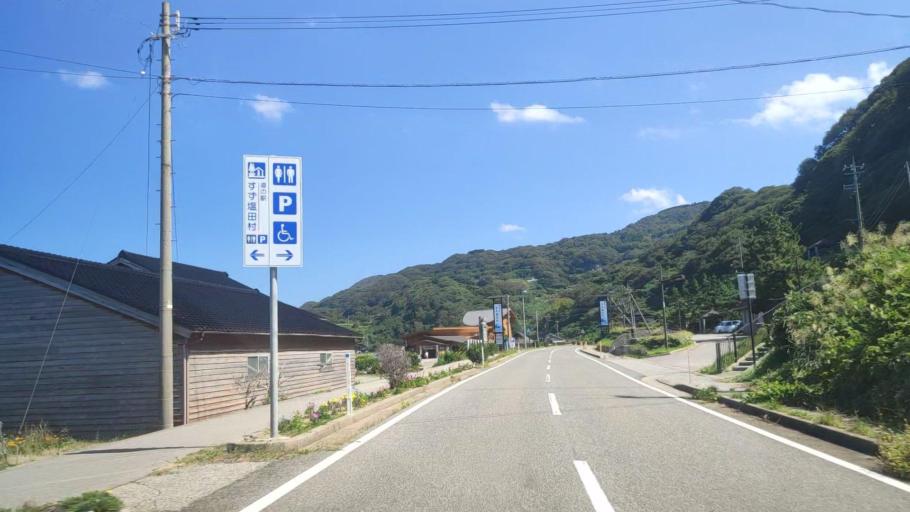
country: JP
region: Ishikawa
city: Nanao
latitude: 37.4862
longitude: 137.1118
